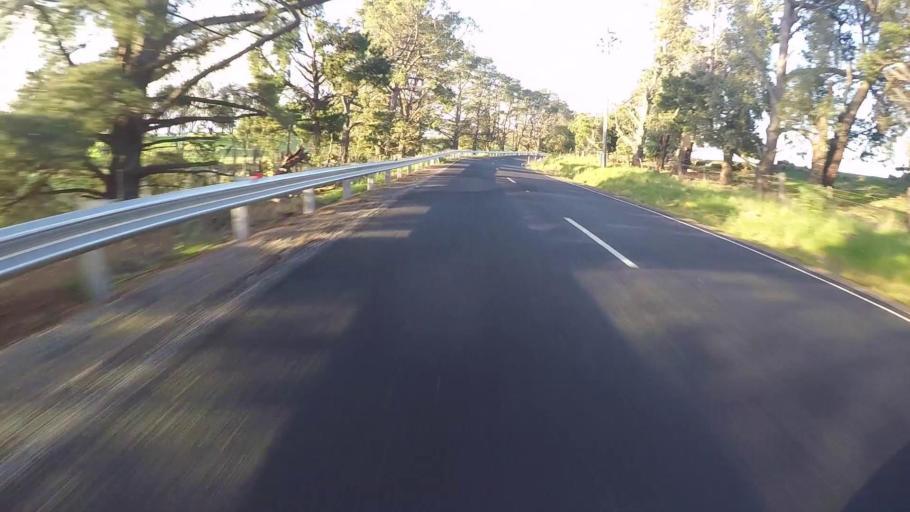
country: AU
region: Victoria
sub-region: Greater Geelong
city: Wandana Heights
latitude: -38.1468
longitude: 144.1818
